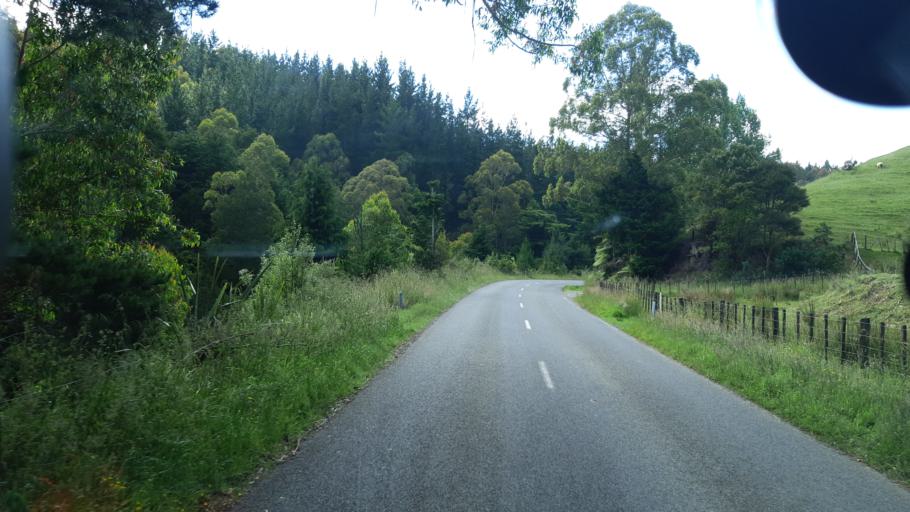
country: NZ
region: Manawatu-Wanganui
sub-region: Rangitikei District
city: Bulls
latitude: -39.9177
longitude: 175.5541
